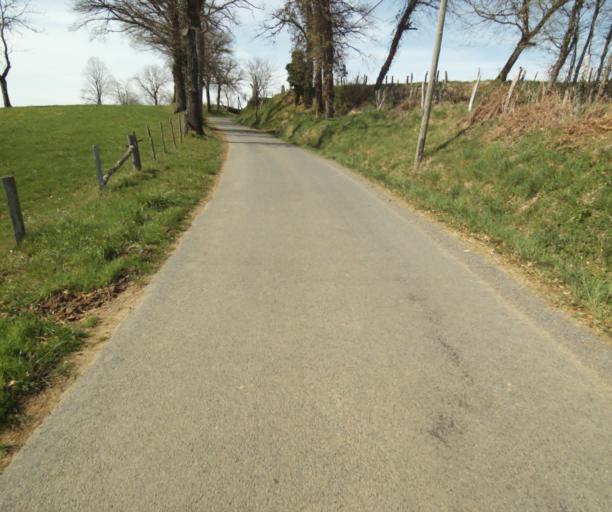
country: FR
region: Limousin
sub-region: Departement de la Correze
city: Naves
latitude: 45.3679
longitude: 1.7780
